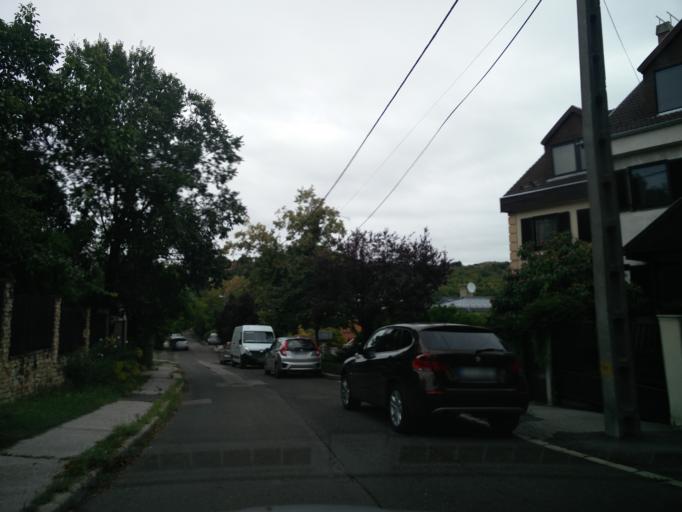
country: HU
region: Budapest
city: Budapest XII. keruelet
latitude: 47.4771
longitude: 19.0095
